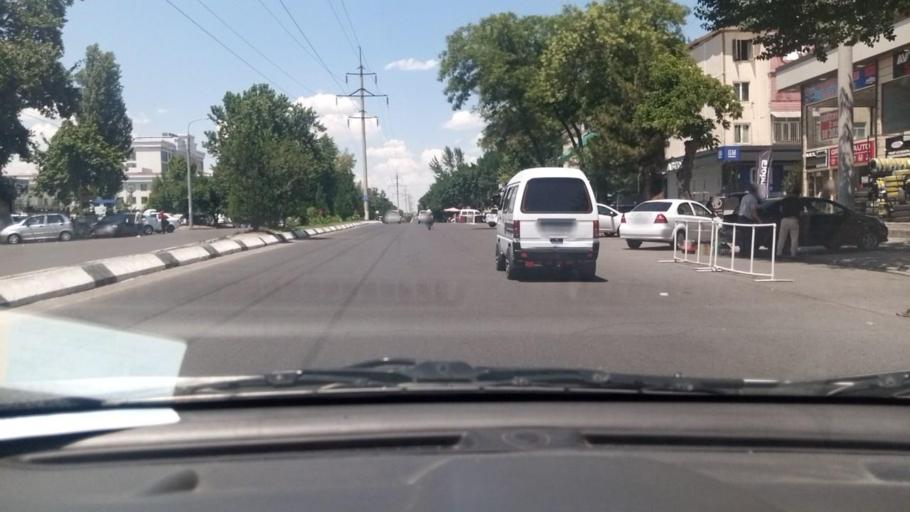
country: UZ
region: Toshkent Shahri
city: Tashkent
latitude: 41.2838
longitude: 69.1947
